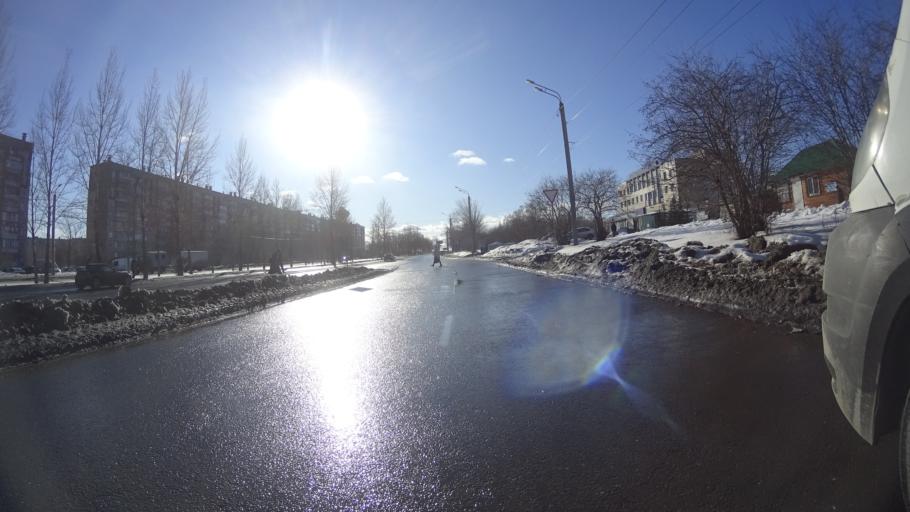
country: RU
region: Chelyabinsk
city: Roshchino
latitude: 55.1817
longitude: 61.2893
